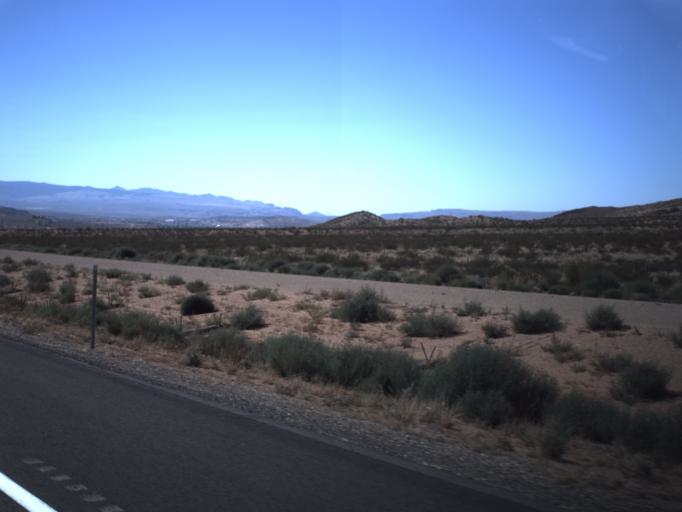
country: US
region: Utah
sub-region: Washington County
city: Washington
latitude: 37.0957
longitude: -113.4691
